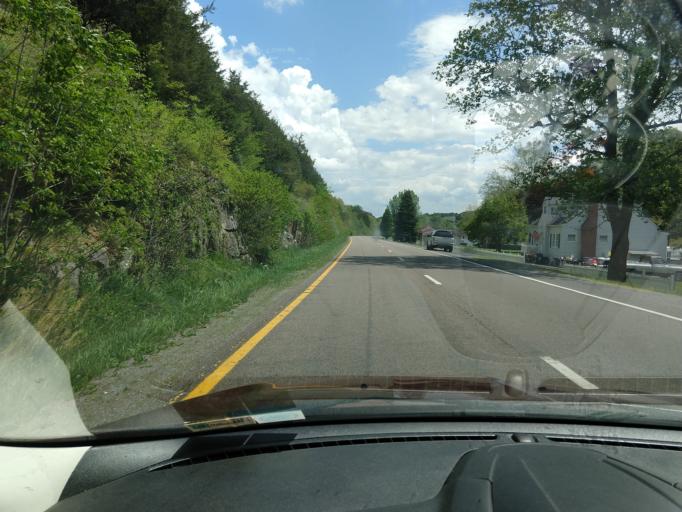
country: US
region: Virginia
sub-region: Tazewell County
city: Raven
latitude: 36.9976
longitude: -81.8258
